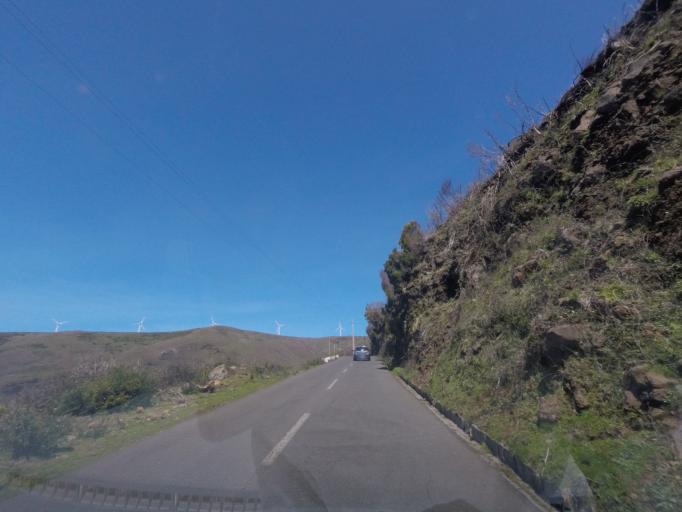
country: PT
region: Madeira
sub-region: Calheta
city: Arco da Calheta
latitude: 32.7355
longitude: -17.1044
